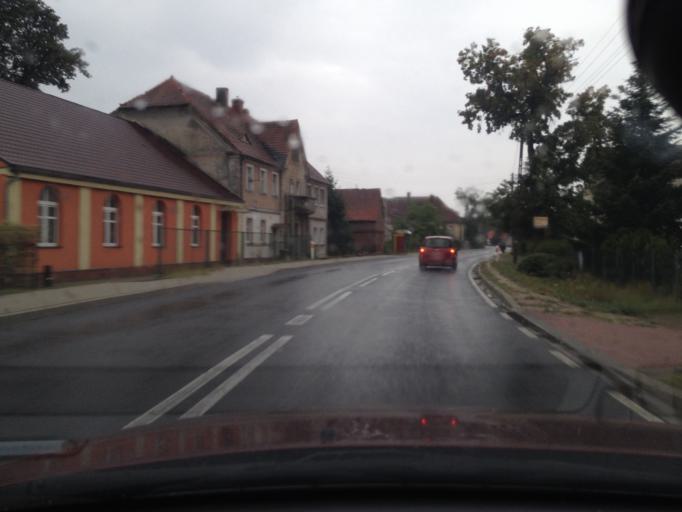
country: PL
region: Lubusz
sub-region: Powiat zaganski
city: Zagan
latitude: 51.6627
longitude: 15.3134
